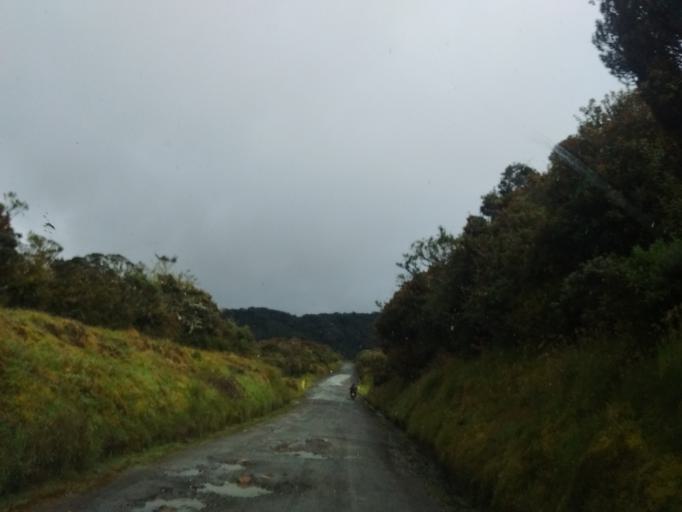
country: CO
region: Cauca
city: Totoro
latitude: 2.3550
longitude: -76.3420
